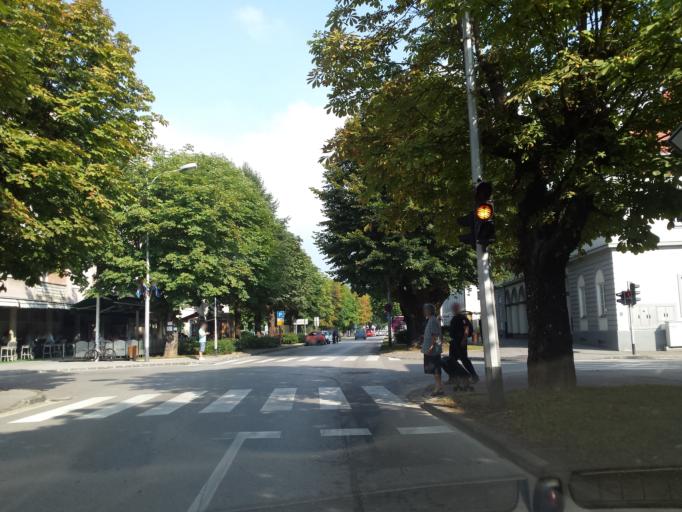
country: HR
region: Karlovacka
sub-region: Grad Ogulin
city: Ogulin
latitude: 45.2651
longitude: 15.2269
